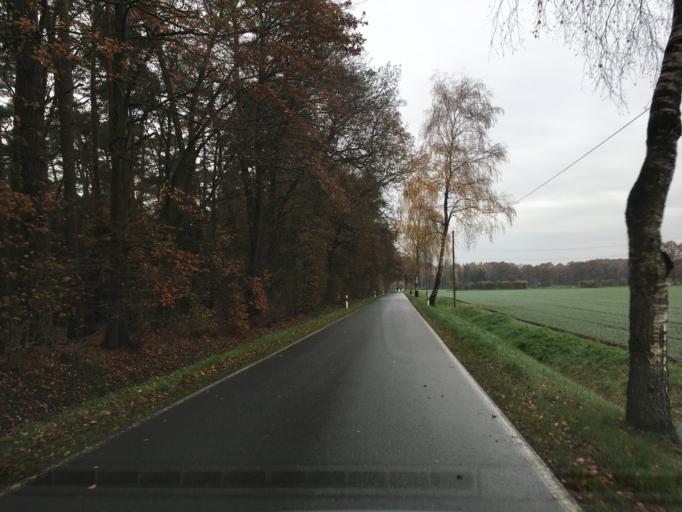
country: DE
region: North Rhine-Westphalia
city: Stadtlohn
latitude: 52.0175
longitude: 6.9743
